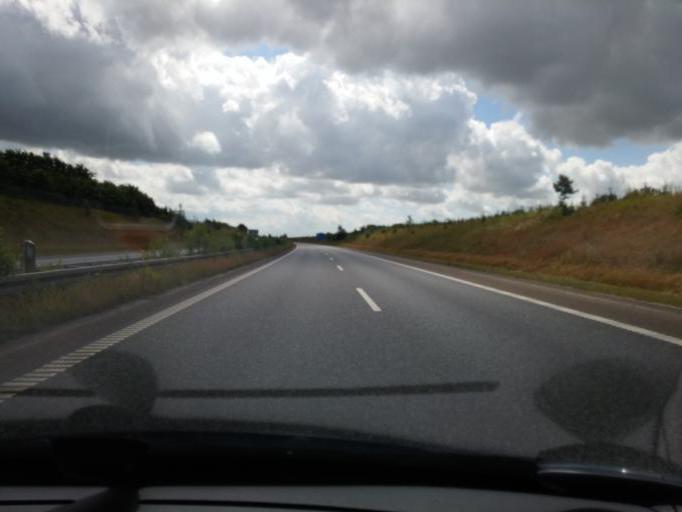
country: DK
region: South Denmark
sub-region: Odense Kommune
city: Hojby
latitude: 55.3166
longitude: 10.4395
